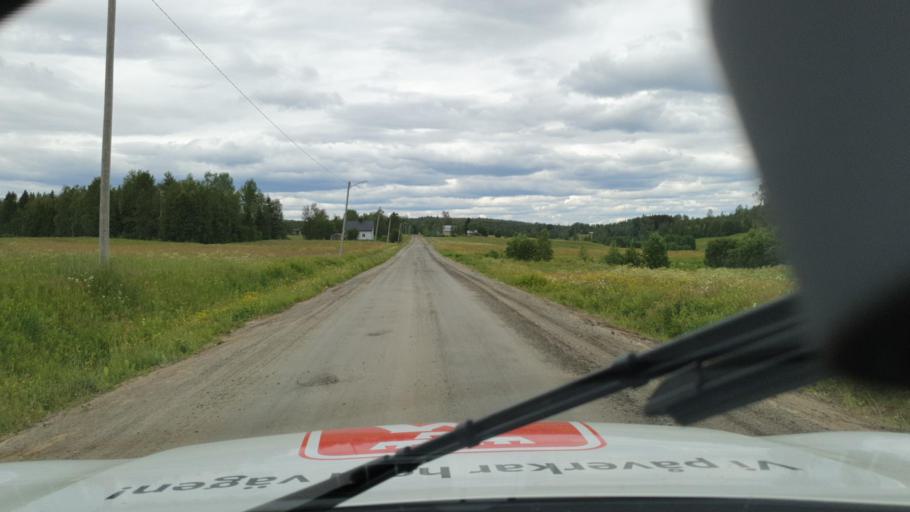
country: SE
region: Vaesterbotten
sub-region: Nordmalings Kommun
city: Nordmaling
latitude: 63.7063
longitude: 19.4377
